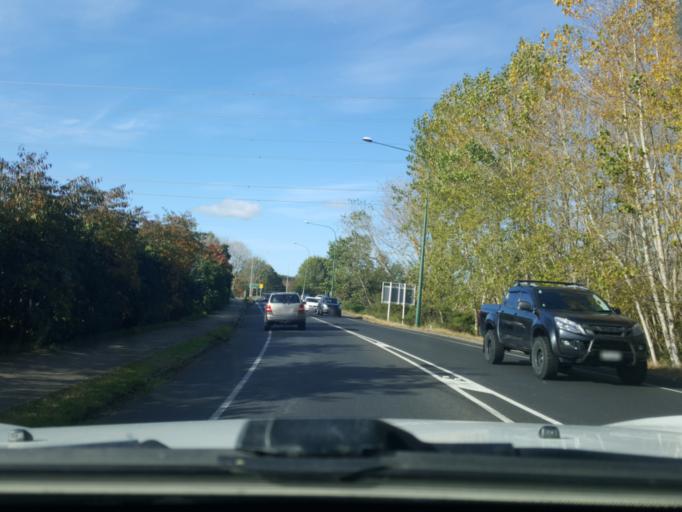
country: NZ
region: Auckland
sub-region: Auckland
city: Muriwai Beach
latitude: -36.7779
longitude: 174.5609
